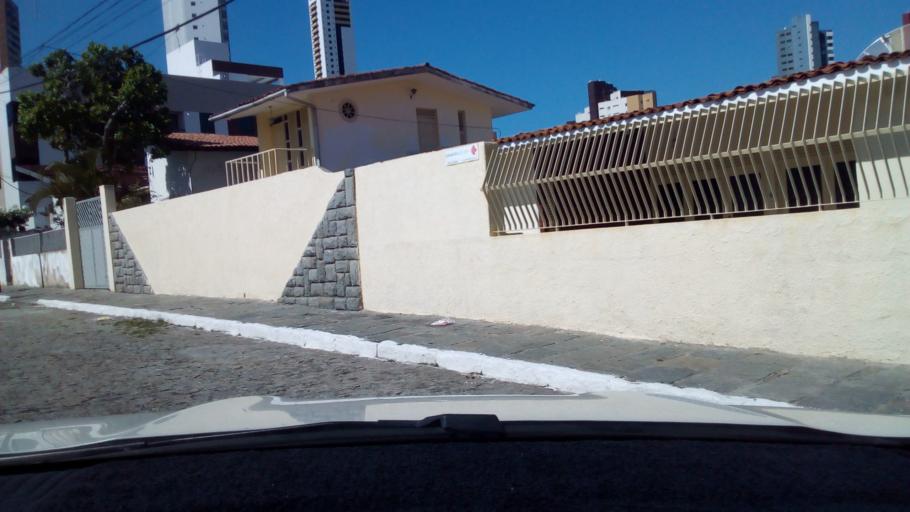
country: BR
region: Paraiba
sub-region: Joao Pessoa
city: Joao Pessoa
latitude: -7.1244
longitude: -34.8358
